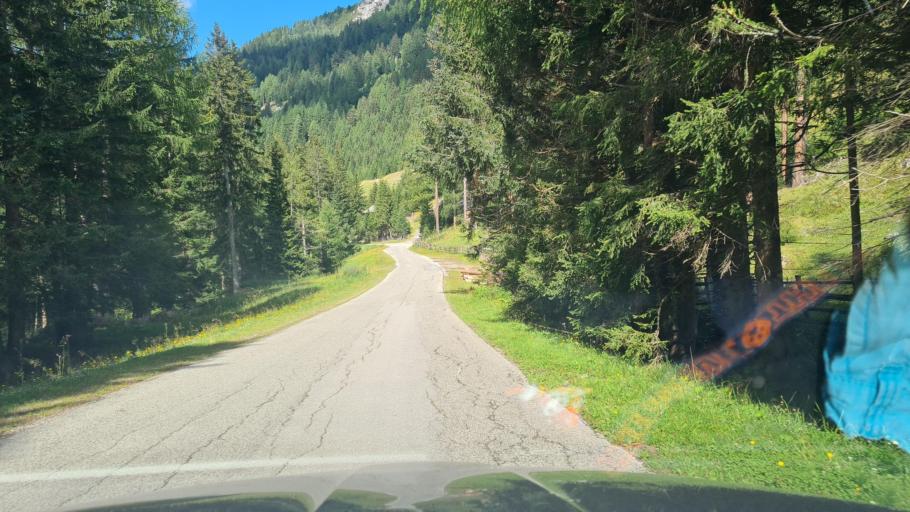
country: AT
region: Salzburg
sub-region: Politischer Bezirk Tamsweg
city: Zederhaus
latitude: 47.1874
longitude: 13.4109
